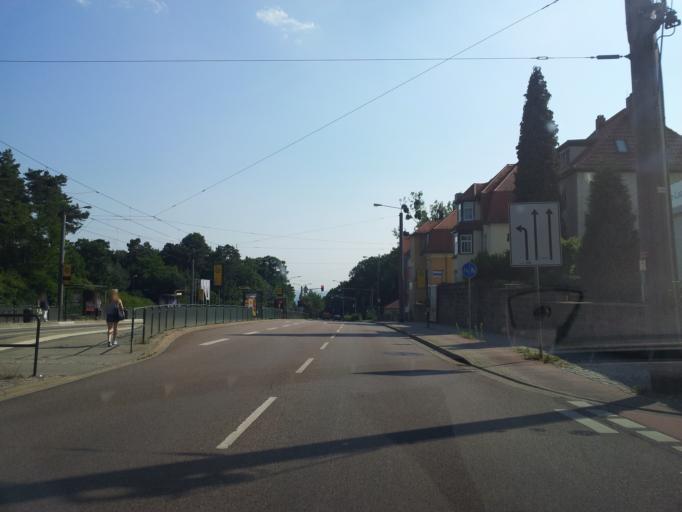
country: DE
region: Saxony
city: Albertstadt
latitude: 51.1085
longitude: 13.7734
